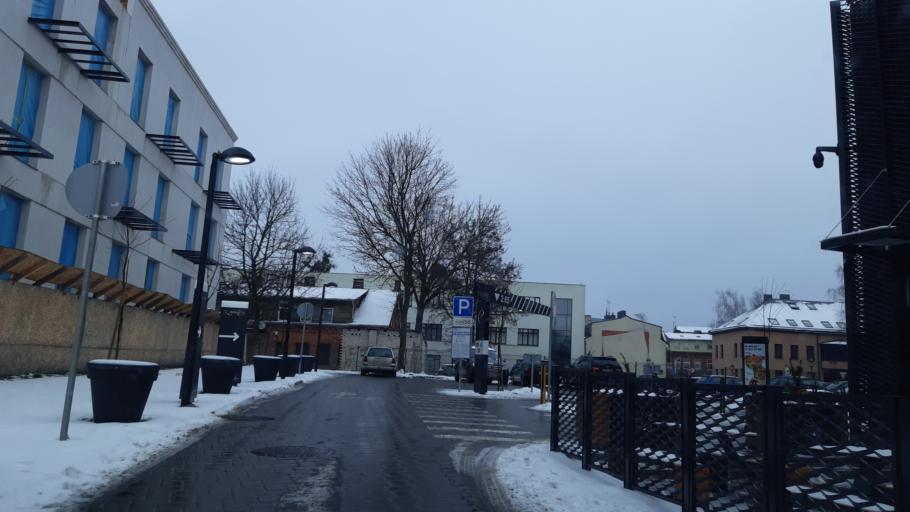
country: LT
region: Kauno apskritis
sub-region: Kaunas
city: Kaunas
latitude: 54.8945
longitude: 23.8978
